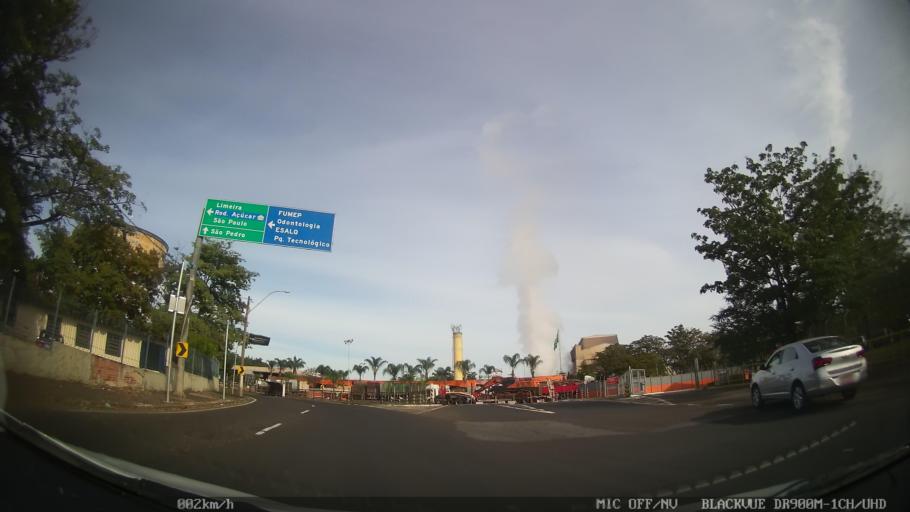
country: BR
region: Sao Paulo
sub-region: Piracicaba
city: Piracicaba
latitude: -22.6980
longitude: -47.6540
